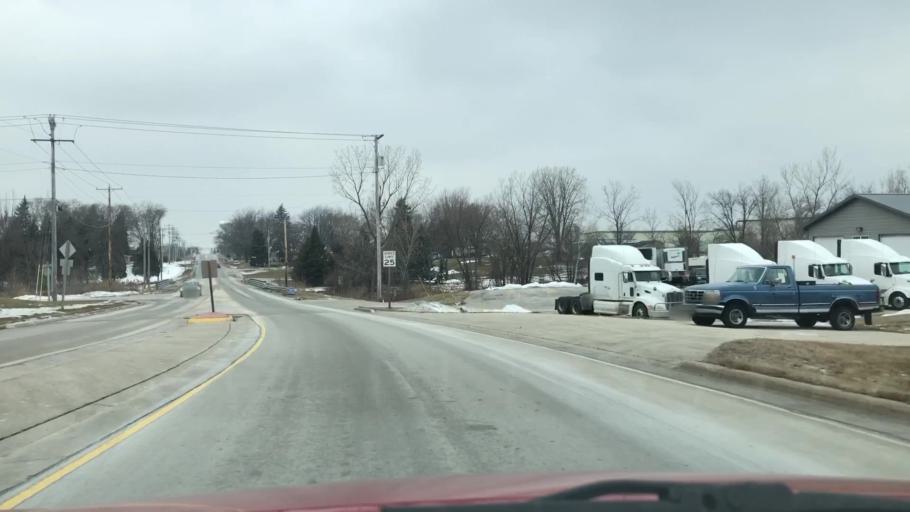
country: US
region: Wisconsin
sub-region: Brown County
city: De Pere
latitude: 44.4575
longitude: -88.0774
